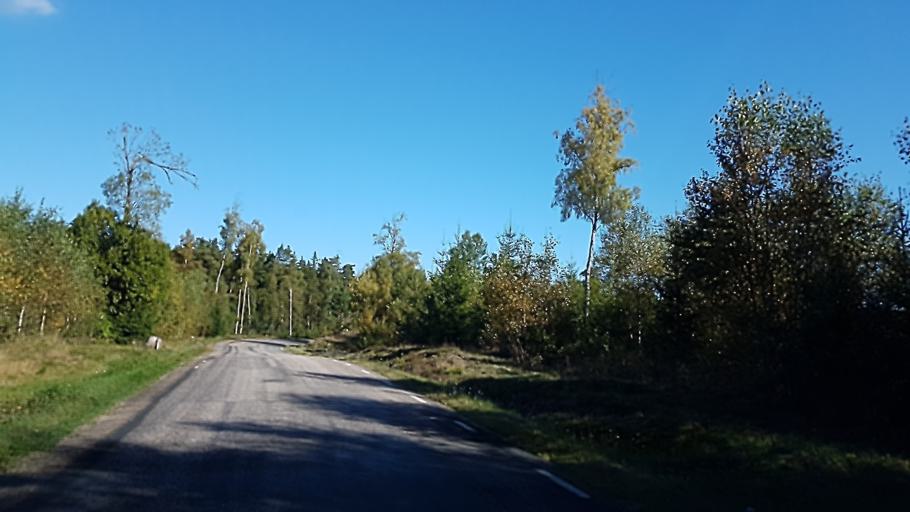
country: SE
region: Kronoberg
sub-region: Ljungby Kommun
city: Ljungby
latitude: 56.8209
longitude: 14.0474
